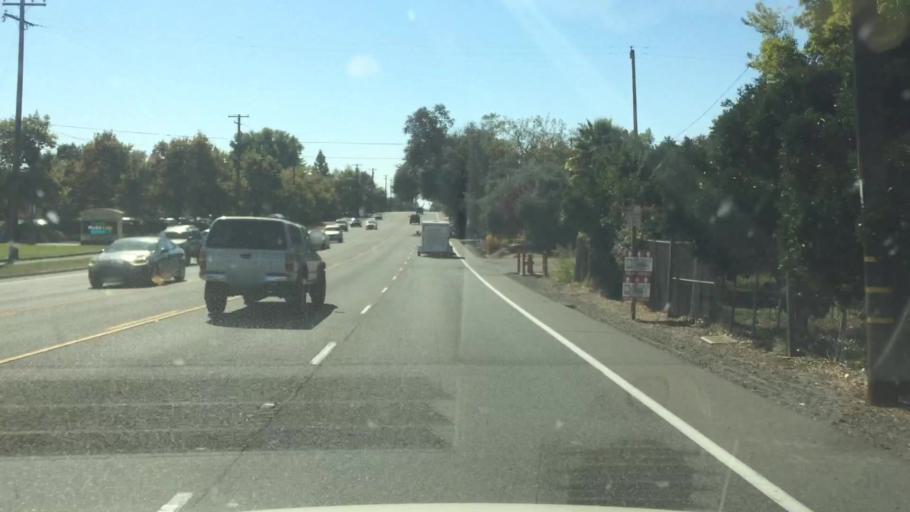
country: US
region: California
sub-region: Sacramento County
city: Orangevale
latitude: 38.6902
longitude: -121.2255
